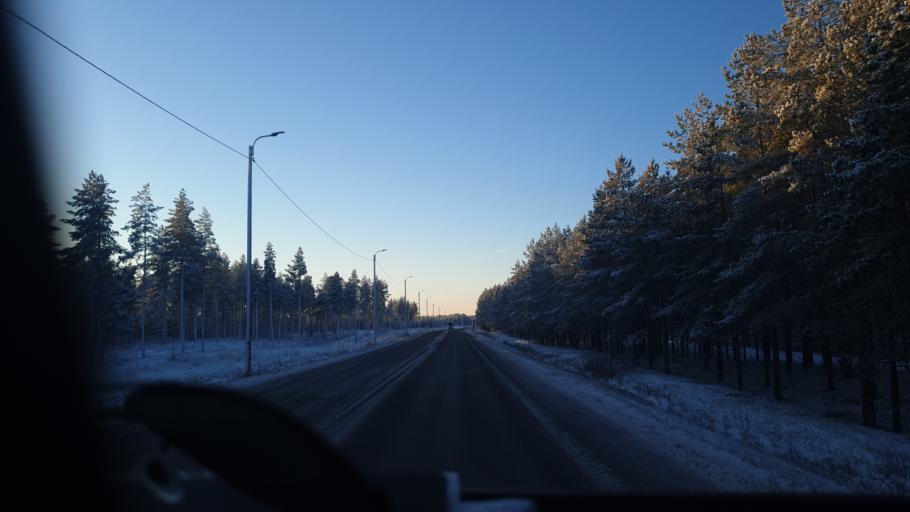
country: FI
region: Northern Ostrobothnia
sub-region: Ylivieska
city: Kalajoki
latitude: 64.2348
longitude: 23.8280
